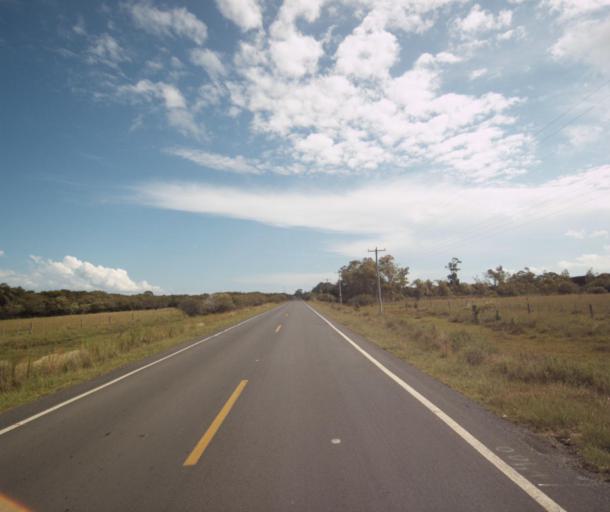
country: BR
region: Rio Grande do Sul
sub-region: Sao Lourenco Do Sul
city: Sao Lourenco do Sul
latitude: -31.6143
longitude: -51.3991
